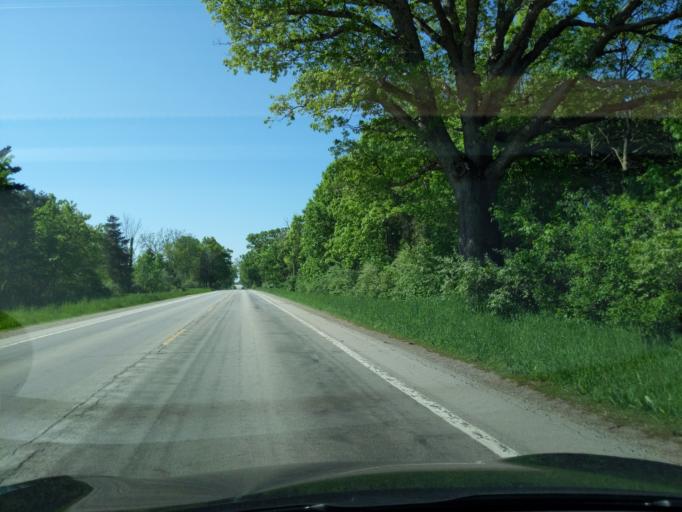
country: US
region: Michigan
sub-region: Ingham County
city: Stockbridge
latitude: 42.4785
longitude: -84.1901
